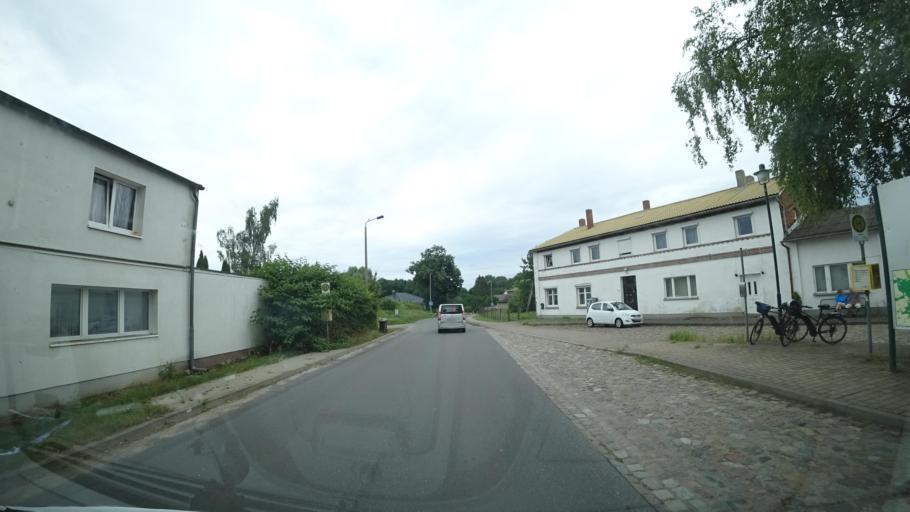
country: DE
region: Mecklenburg-Vorpommern
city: Sehlen
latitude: 54.3398
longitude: 13.4185
